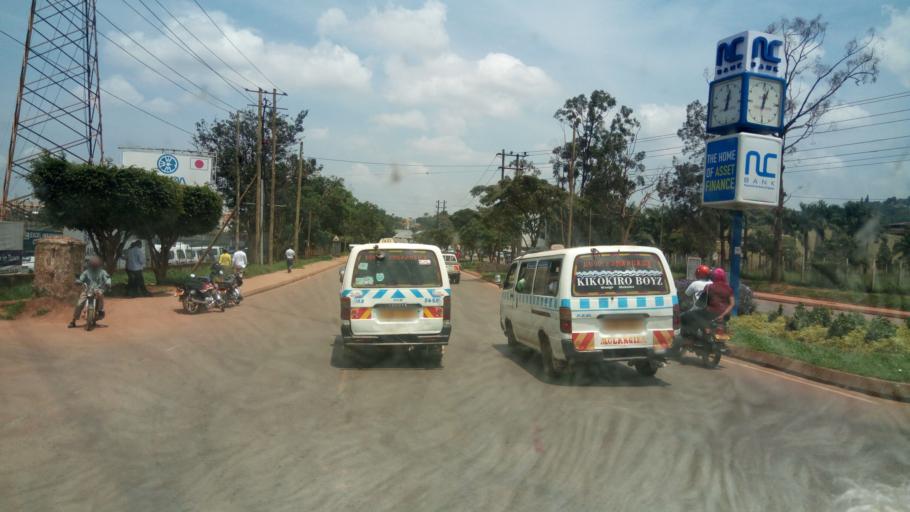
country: UG
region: Central Region
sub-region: Kampala District
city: Kampala
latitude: 0.3263
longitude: 32.6097
